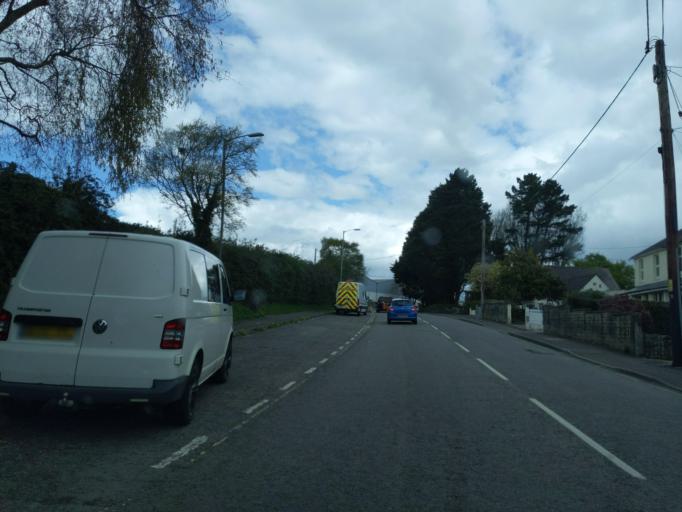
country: GB
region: England
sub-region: Cornwall
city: Saltash
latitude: 50.4152
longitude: -4.2335
